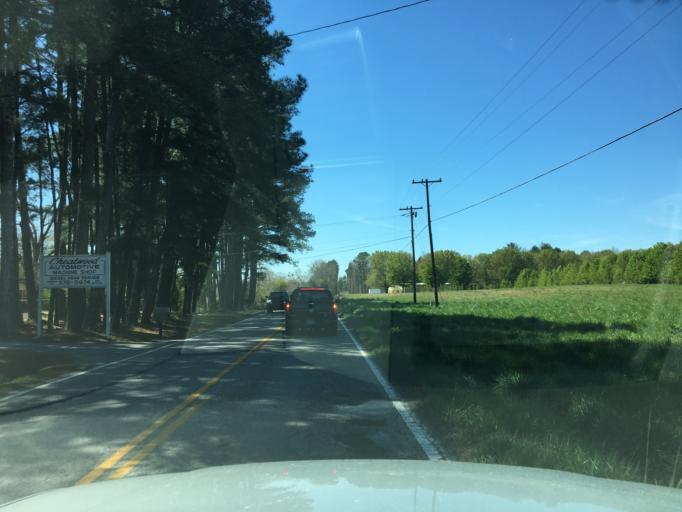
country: US
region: South Carolina
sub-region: Spartanburg County
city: Roebuck
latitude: 34.8825
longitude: -81.9841
